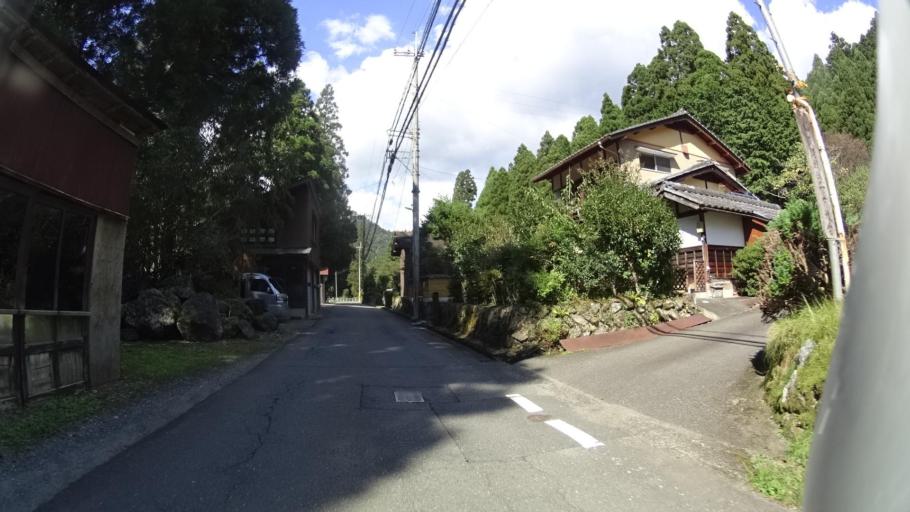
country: JP
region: Shiga Prefecture
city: Kitahama
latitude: 35.2287
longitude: 135.7803
